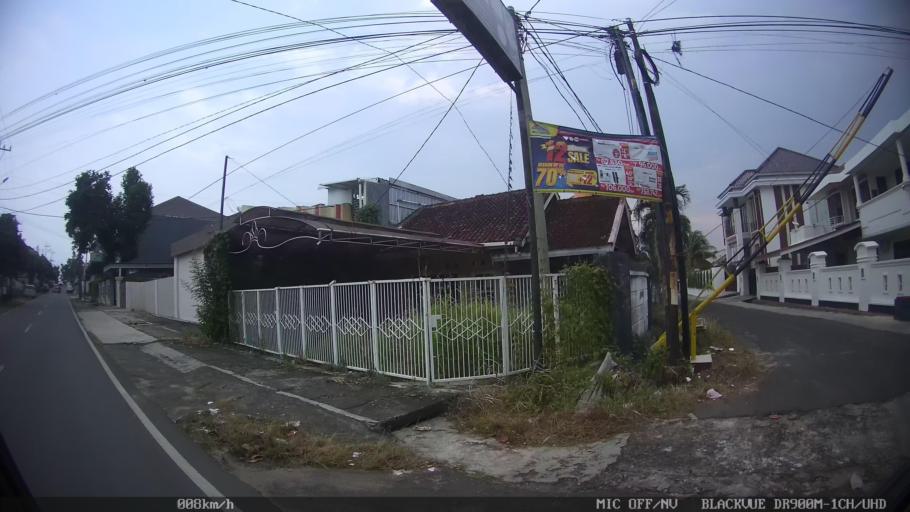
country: ID
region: Lampung
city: Bandarlampung
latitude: -5.4233
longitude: 105.2665
